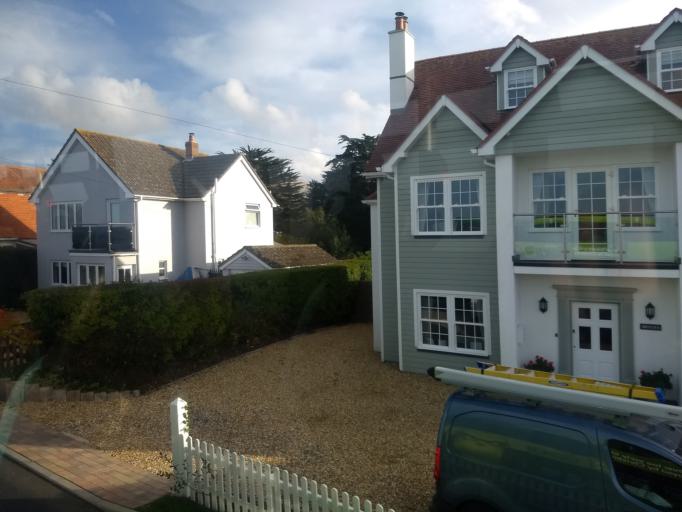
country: GB
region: England
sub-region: Isle of Wight
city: Yarmouth
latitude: 50.7065
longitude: -1.4861
